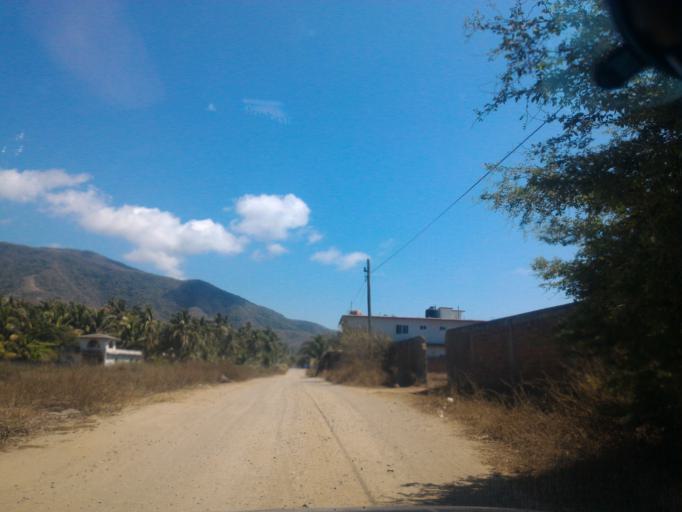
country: MX
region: Michoacan
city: Coahuayana Viejo
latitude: 18.5852
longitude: -103.6775
